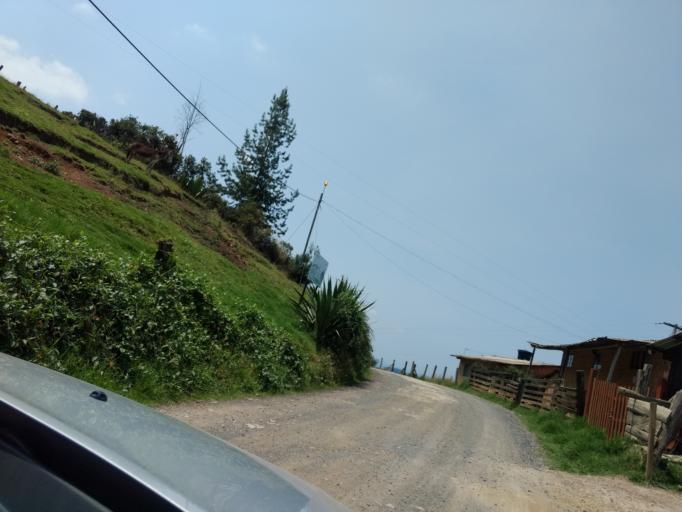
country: CO
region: Boyaca
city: Raquira
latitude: 5.5074
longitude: -73.7186
